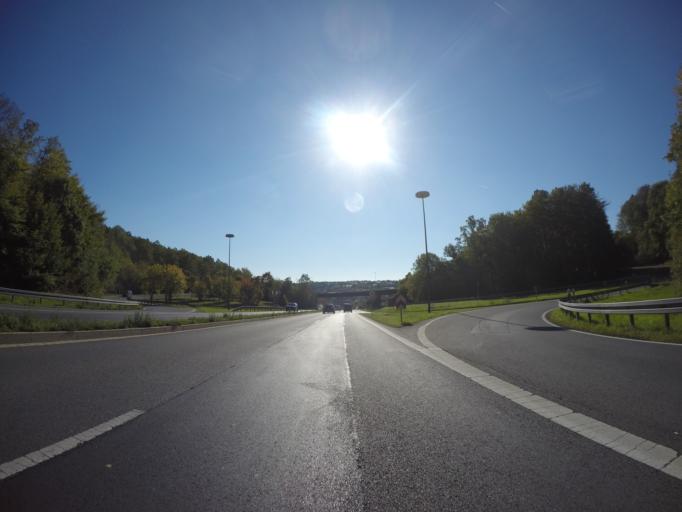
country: DE
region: Bavaria
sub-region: Regierungsbezirk Unterfranken
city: Hochberg
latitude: 49.7883
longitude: 9.8753
